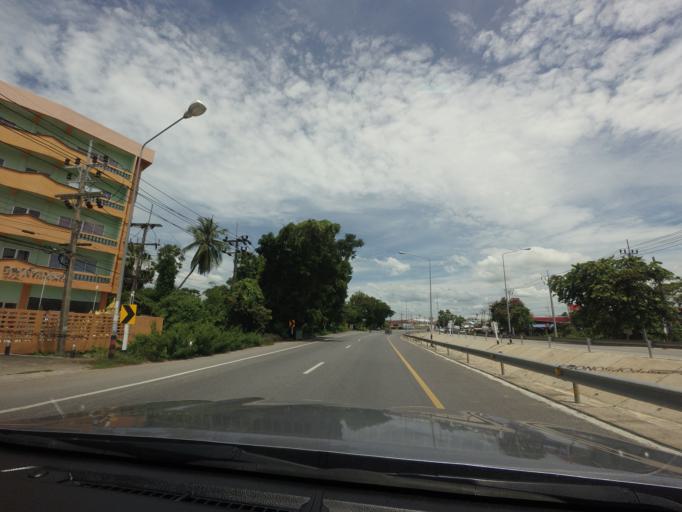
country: TH
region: Songkhla
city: Ban Mai
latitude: 7.2117
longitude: 100.5572
